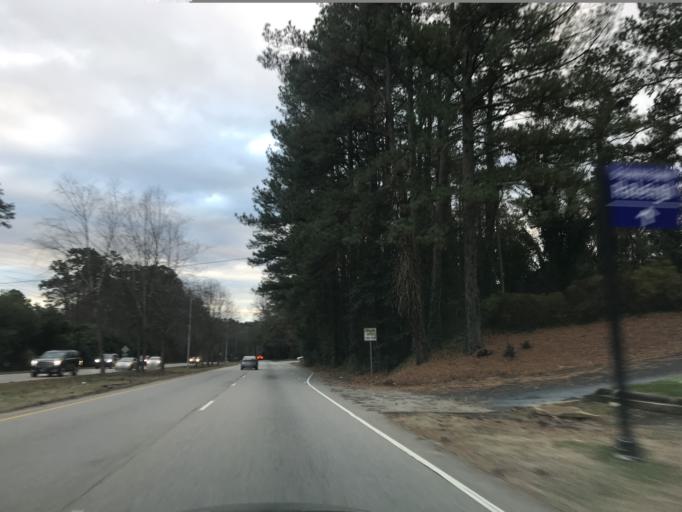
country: US
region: North Carolina
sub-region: Wake County
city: West Raleigh
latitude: 35.8208
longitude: -78.6643
